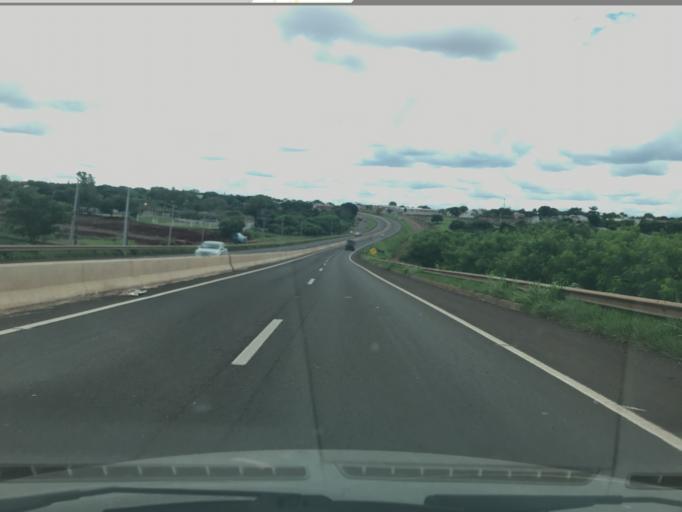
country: BR
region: Parana
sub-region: Maringa
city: Maringa
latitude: -23.3720
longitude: -51.9257
